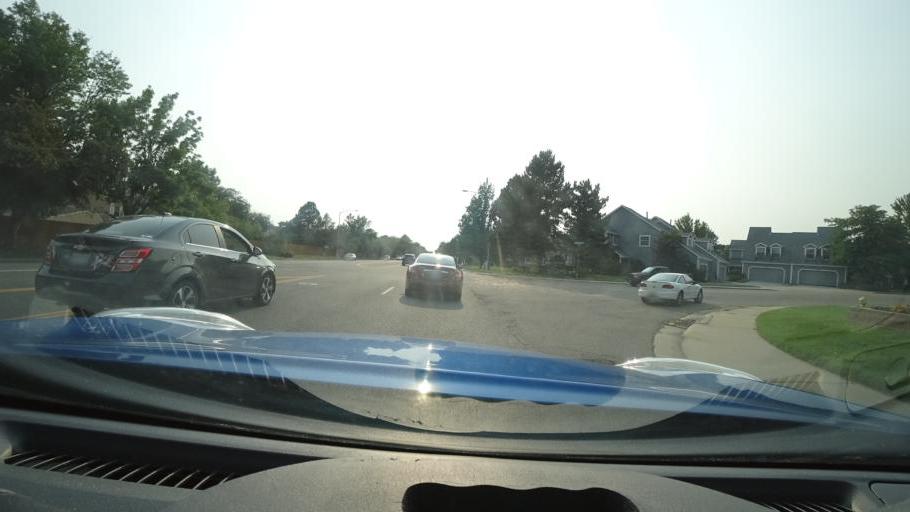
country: US
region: Colorado
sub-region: Adams County
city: Aurora
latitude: 39.6677
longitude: -104.8364
